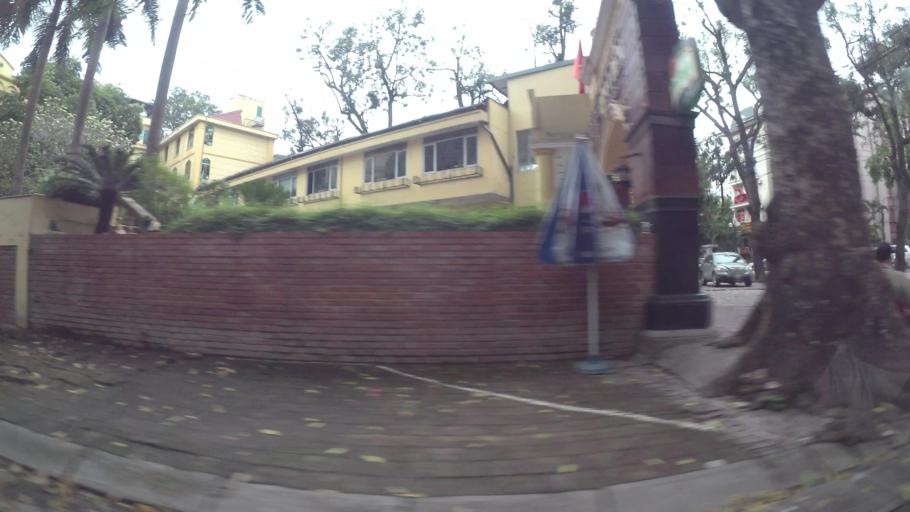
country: VN
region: Ha Noi
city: Hai BaTrung
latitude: 21.0182
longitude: 105.8590
